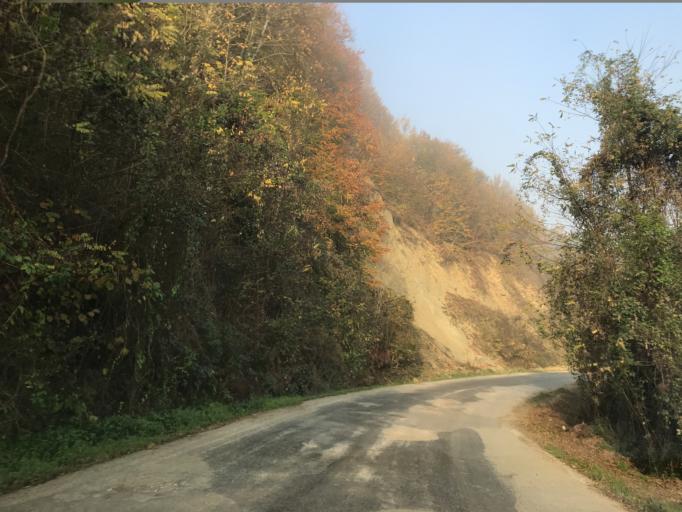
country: TR
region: Duzce
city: Cumayeri
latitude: 40.9106
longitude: 30.9450
